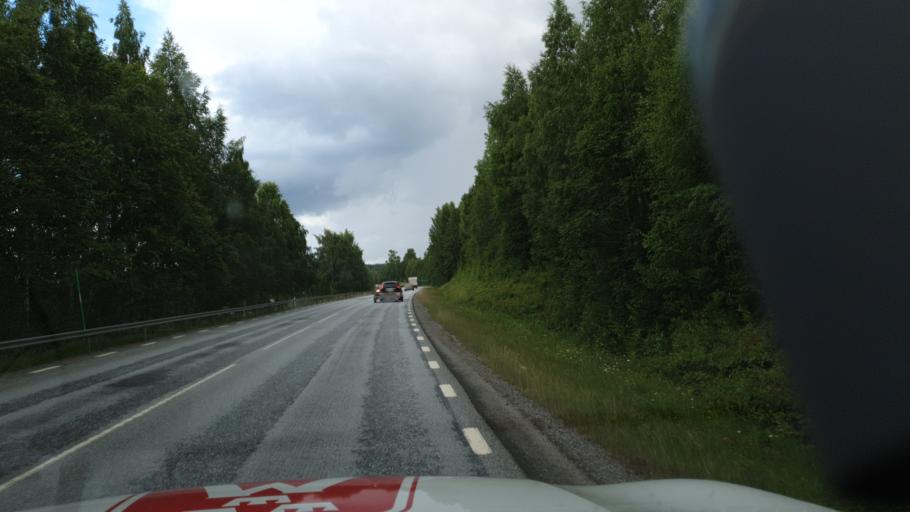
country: SE
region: Vaesterbotten
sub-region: Vannas Kommun
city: Vannasby
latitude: 64.0043
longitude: 20.0349
